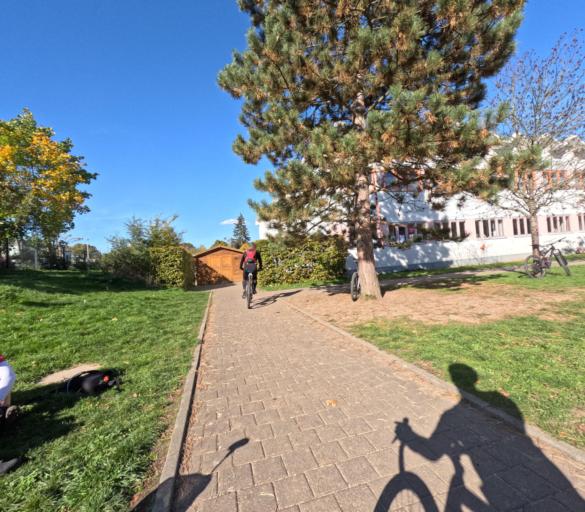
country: DE
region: Saxony
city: Ottendorf-Okrilla
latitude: 51.1244
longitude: 13.8394
